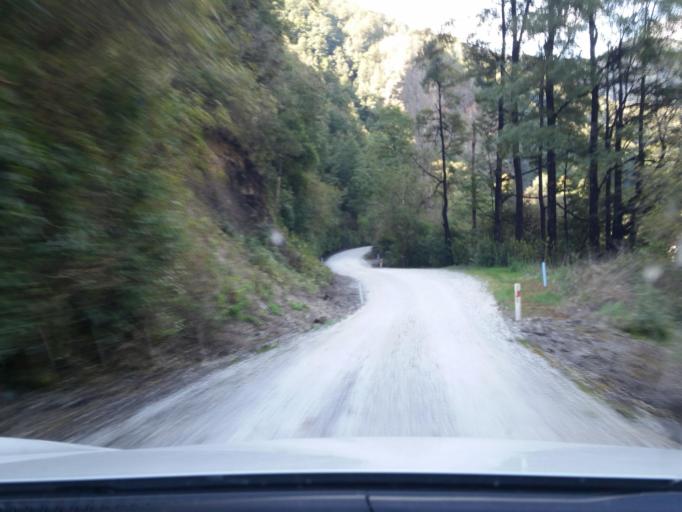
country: NZ
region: West Coast
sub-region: Buller District
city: Westport
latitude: -41.7705
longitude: 172.2283
